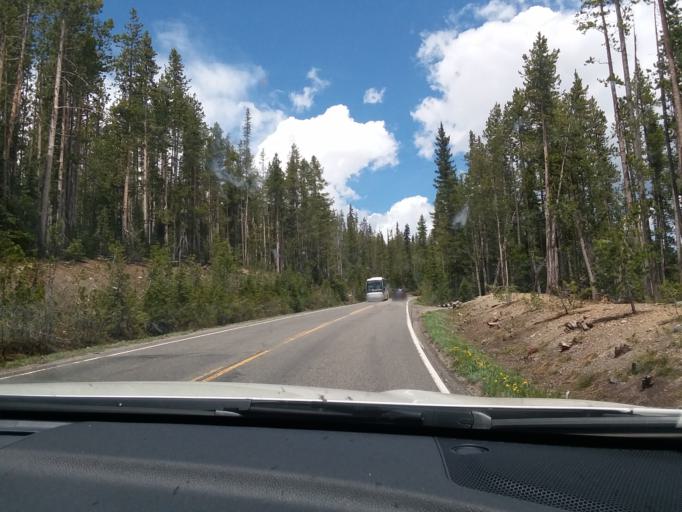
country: US
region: Montana
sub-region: Gallatin County
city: West Yellowstone
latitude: 44.1931
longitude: -110.6581
